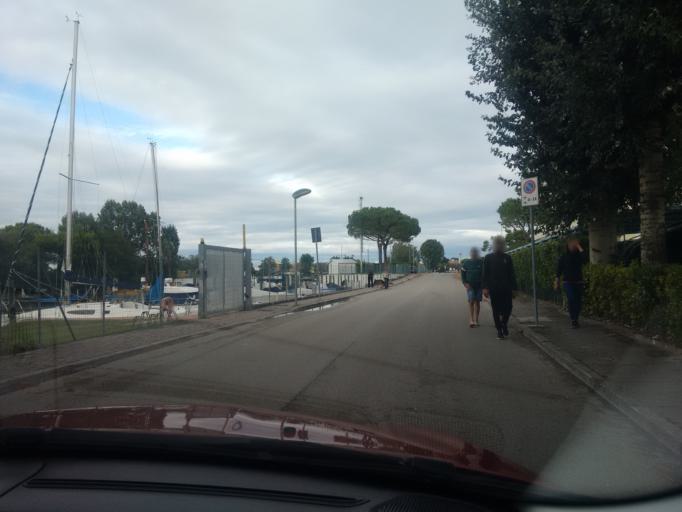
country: IT
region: Veneto
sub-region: Provincia di Venezia
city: Caorle
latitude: 45.5892
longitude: 12.8602
